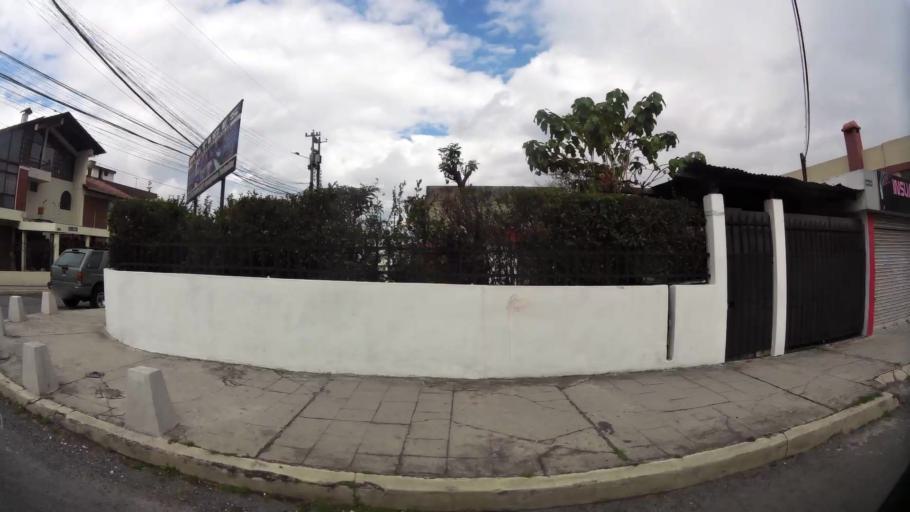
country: EC
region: Pichincha
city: Quito
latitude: -0.1604
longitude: -78.4812
